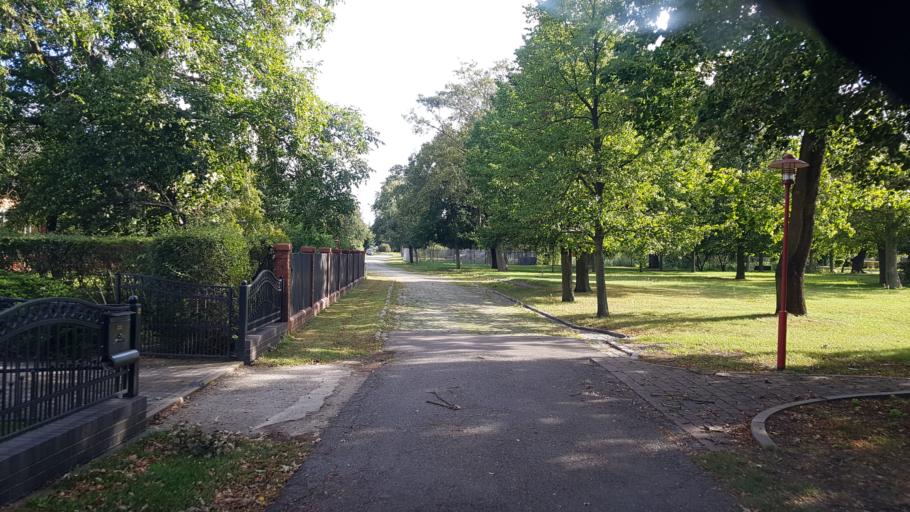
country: DE
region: Saxony
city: Schleife
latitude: 51.5740
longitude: 14.4748
